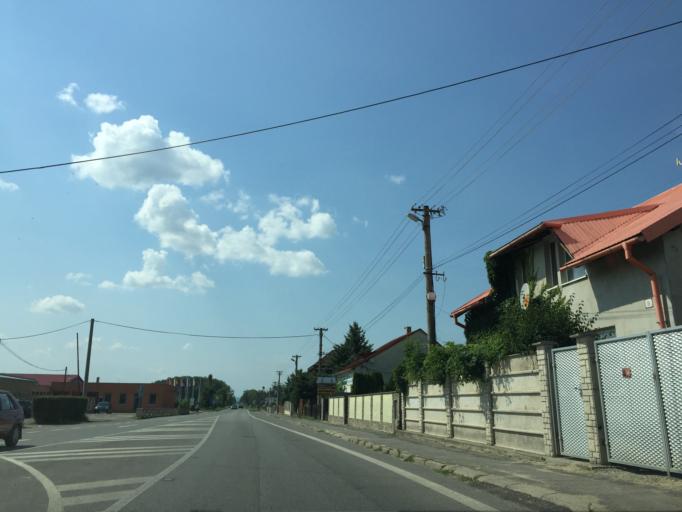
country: SK
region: Kosicky
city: Sobrance
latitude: 48.7472
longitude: 22.1750
